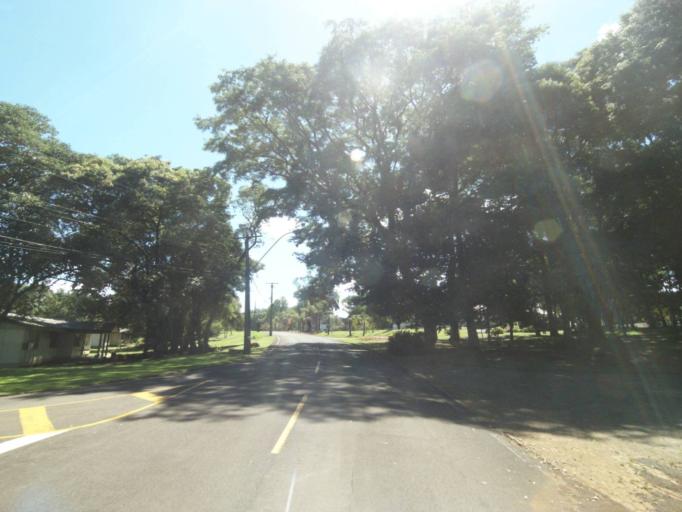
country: BR
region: Parana
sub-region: Chopinzinho
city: Chopinzinho
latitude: -25.7992
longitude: -52.0996
